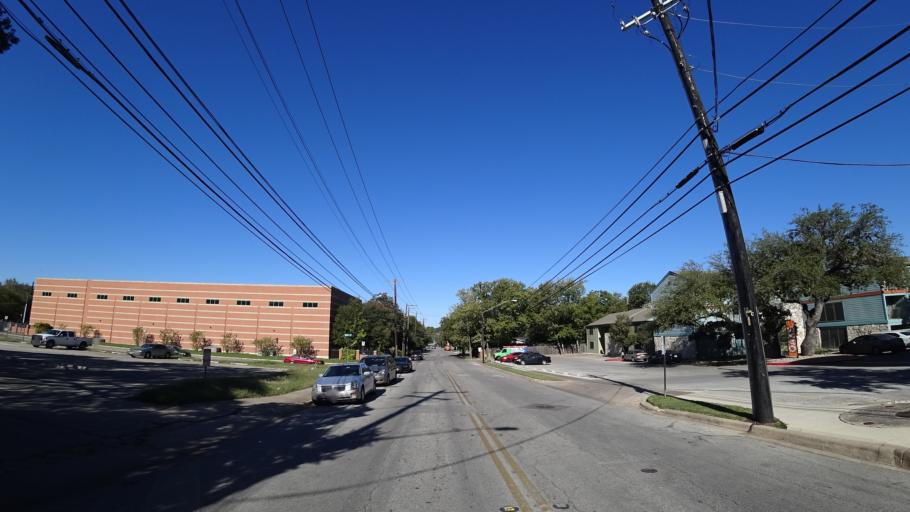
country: US
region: Texas
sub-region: Travis County
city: Austin
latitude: 30.2360
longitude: -97.7574
